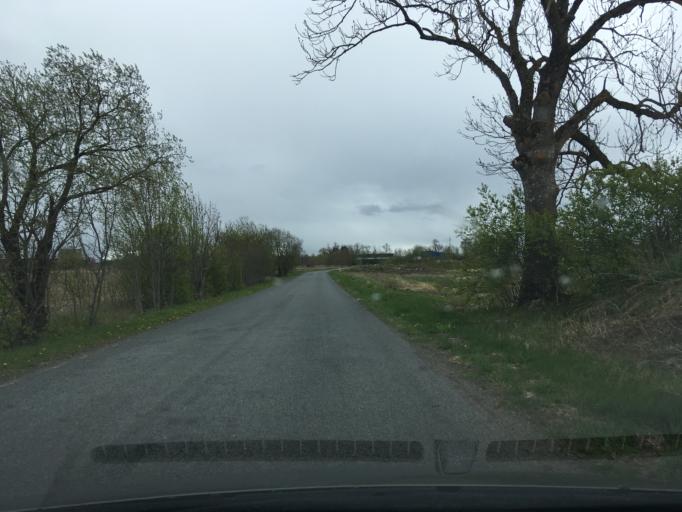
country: EE
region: Harju
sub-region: Rae vald
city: Vaida
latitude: 59.2963
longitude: 24.9720
